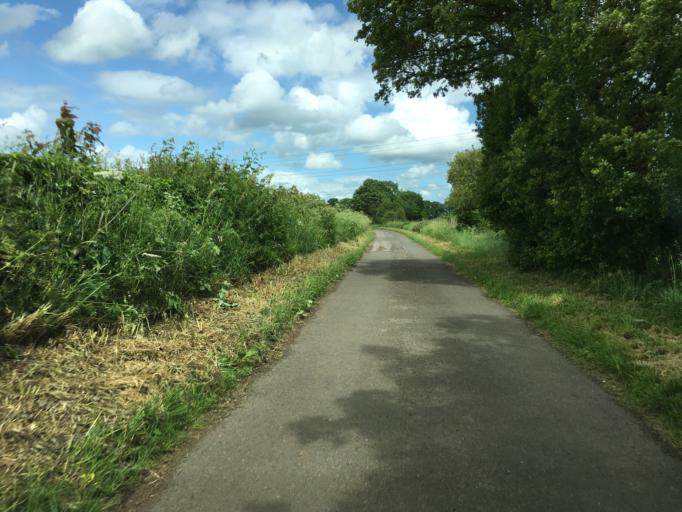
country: GB
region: England
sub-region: Gloucestershire
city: Cirencester
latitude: 51.7623
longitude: -1.9835
